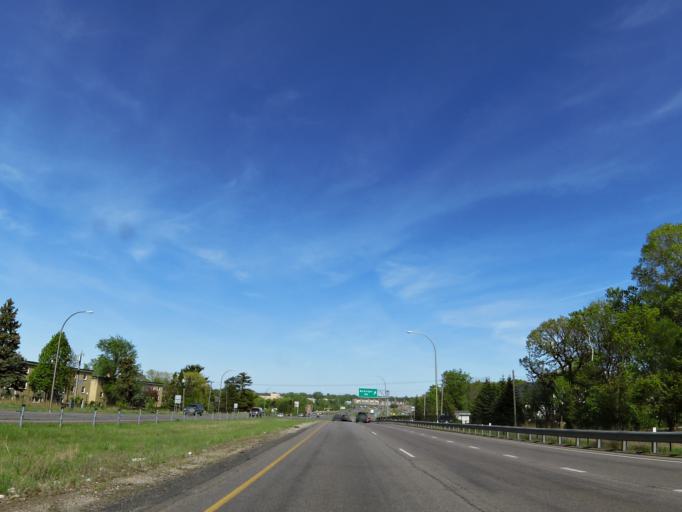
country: US
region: Minnesota
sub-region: Ramsey County
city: North Saint Paul
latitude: 45.0117
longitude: -93.0143
